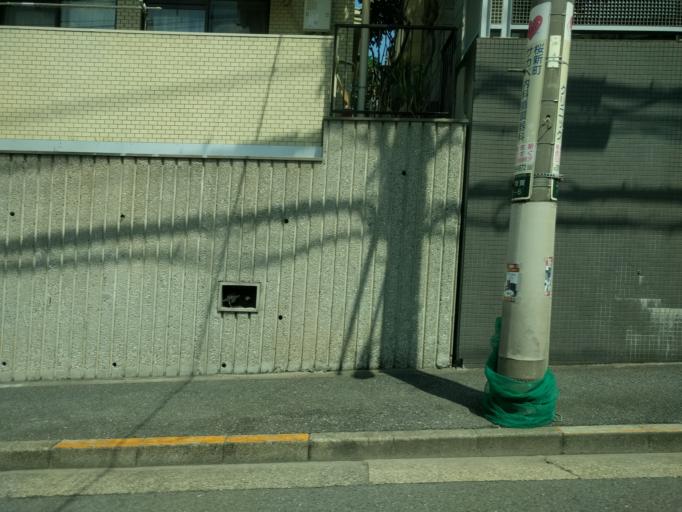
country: JP
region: Tokyo
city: Tokyo
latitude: 35.6313
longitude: 139.6353
